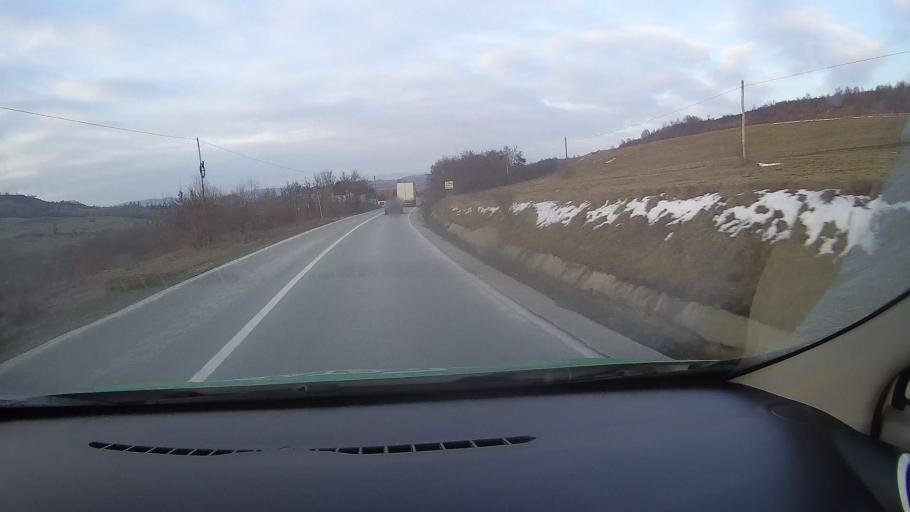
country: RO
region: Harghita
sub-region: Comuna Simonesti
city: Simonesti
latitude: 46.3261
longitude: 25.1021
